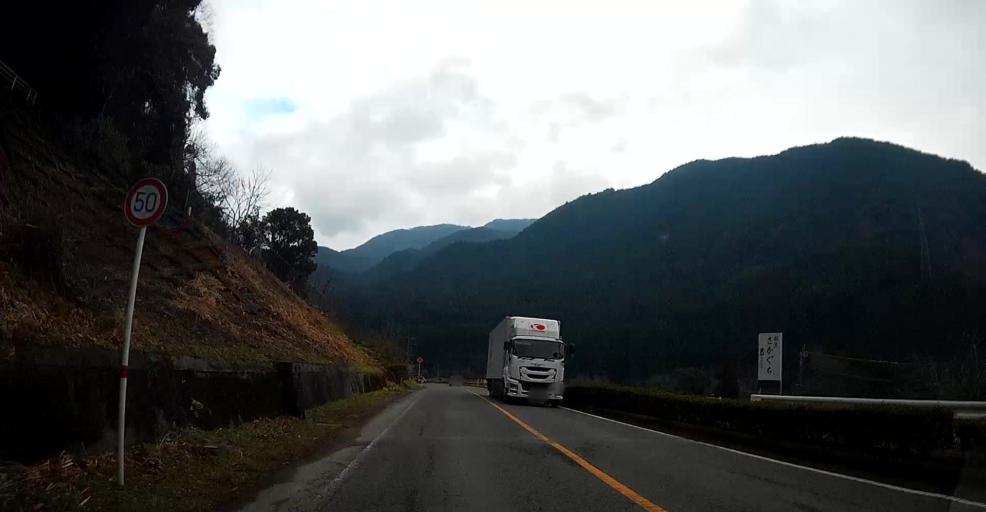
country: JP
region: Kumamoto
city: Matsubase
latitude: 32.6145
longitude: 130.8442
